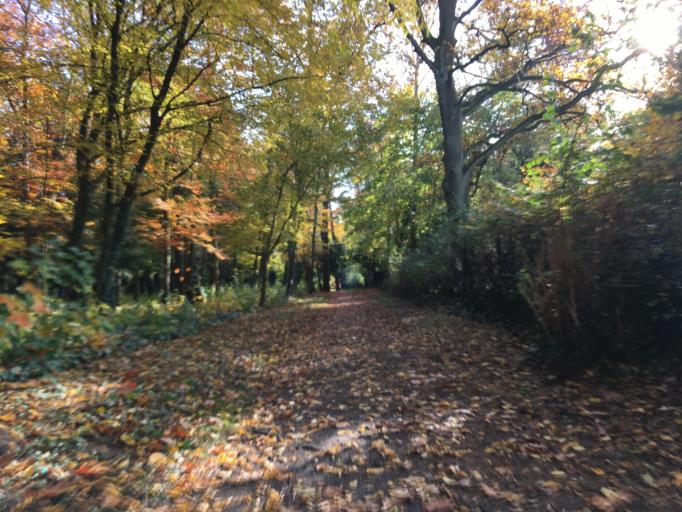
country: DE
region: Berlin
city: Frohnau
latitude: 52.6406
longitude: 13.2880
